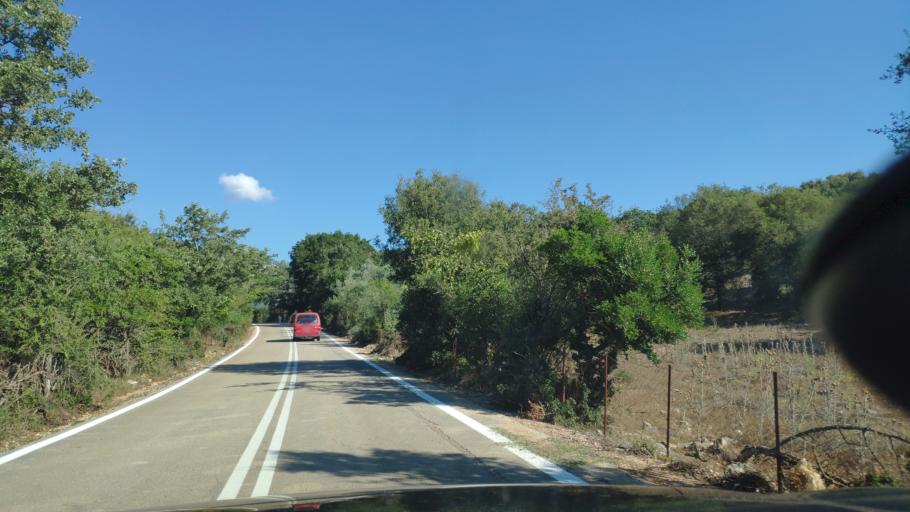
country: GR
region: West Greece
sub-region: Nomos Aitolias kai Akarnanias
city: Fitiai
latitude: 38.6871
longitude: 21.1175
